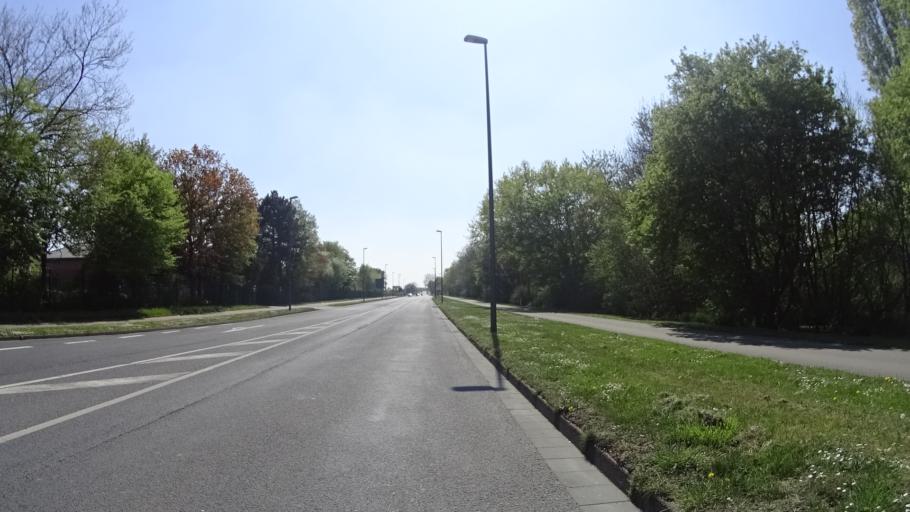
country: DE
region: North Rhine-Westphalia
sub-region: Regierungsbezirk Dusseldorf
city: Krefeld
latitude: 51.3788
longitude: 6.6340
